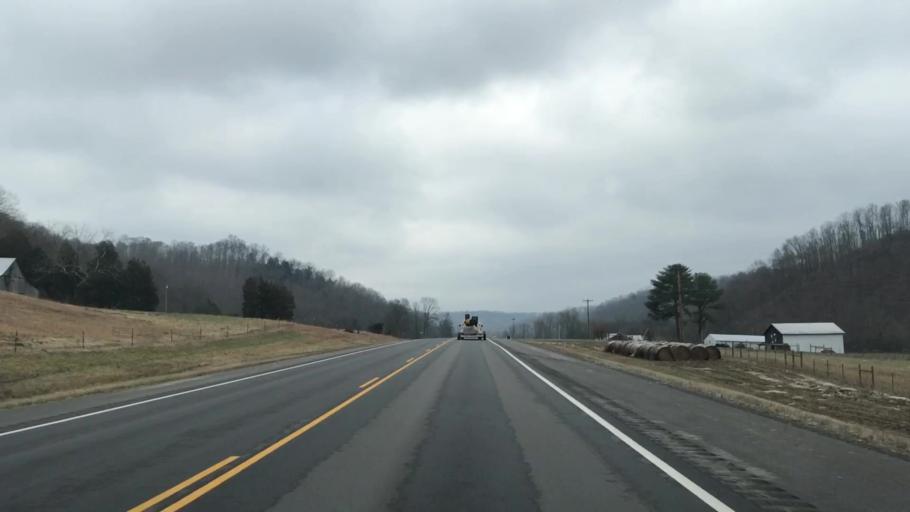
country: US
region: Kentucky
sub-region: Cumberland County
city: Burkesville
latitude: 36.8792
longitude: -85.4011
